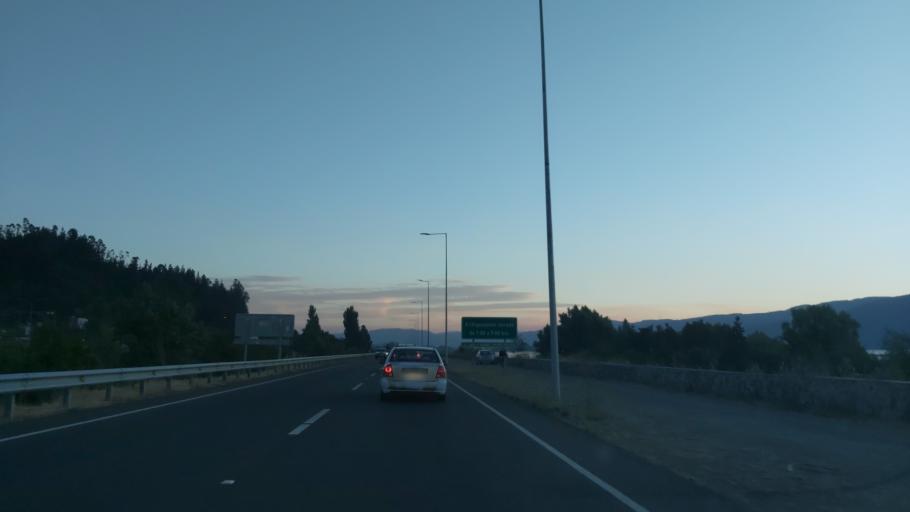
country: CL
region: Biobio
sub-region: Provincia de Concepcion
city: Chiguayante
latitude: -36.8823
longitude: -73.0387
